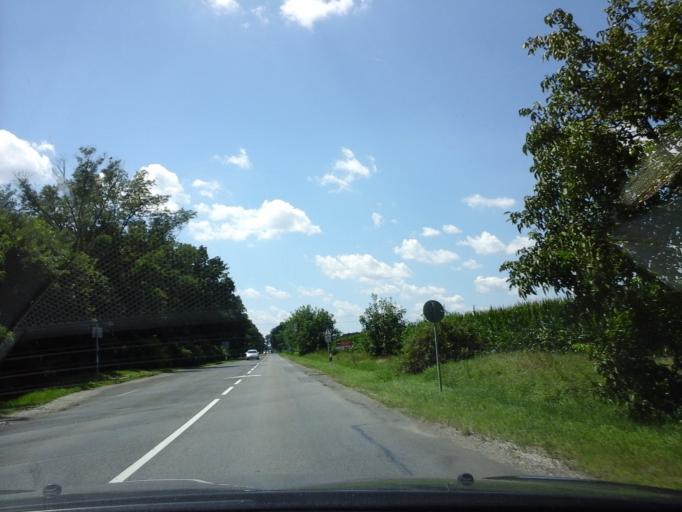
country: HU
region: Hajdu-Bihar
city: Hajduszoboszlo
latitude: 47.4558
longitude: 21.4235
